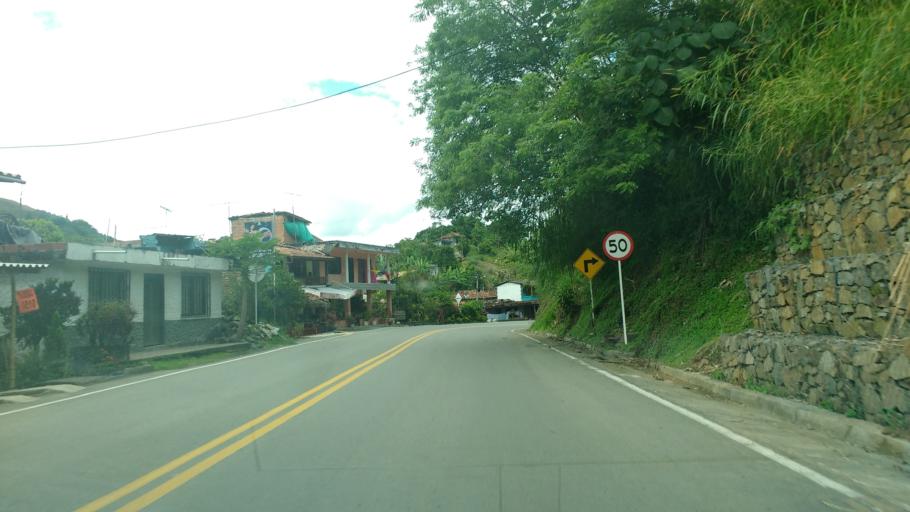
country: CO
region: Antioquia
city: Titiribi
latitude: 6.0629
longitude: -75.7504
